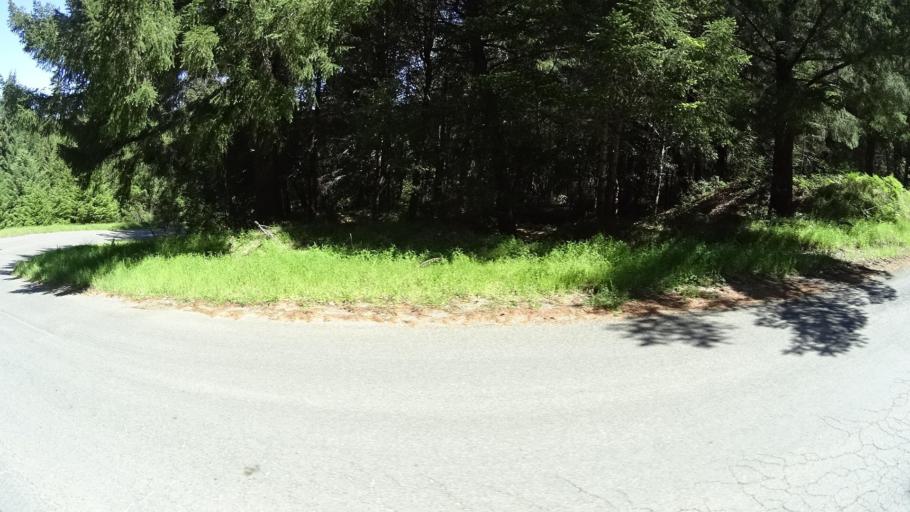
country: US
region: California
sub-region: Humboldt County
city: Redway
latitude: 40.1353
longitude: -123.9902
